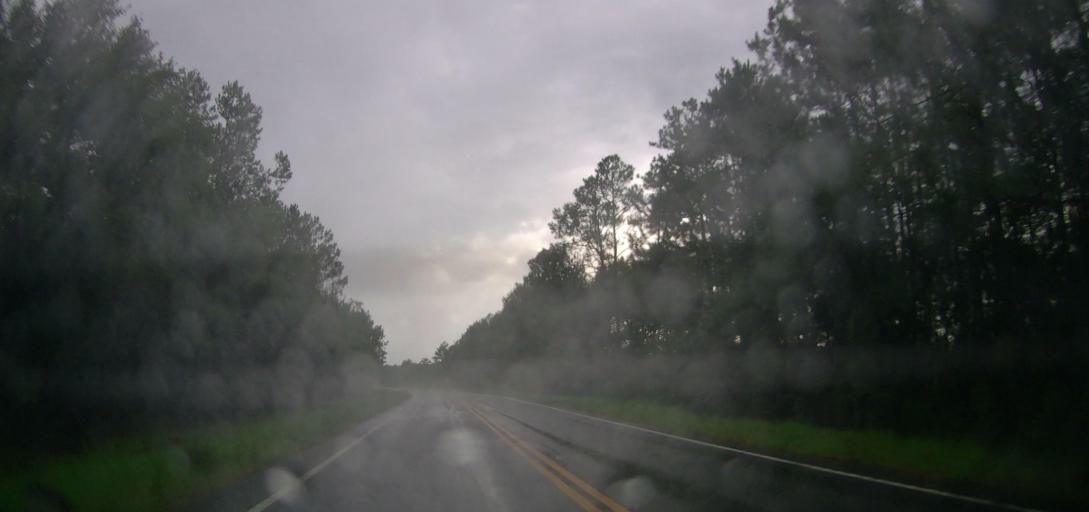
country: US
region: Georgia
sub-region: Brantley County
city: Nahunta
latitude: 31.3431
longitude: -81.7920
